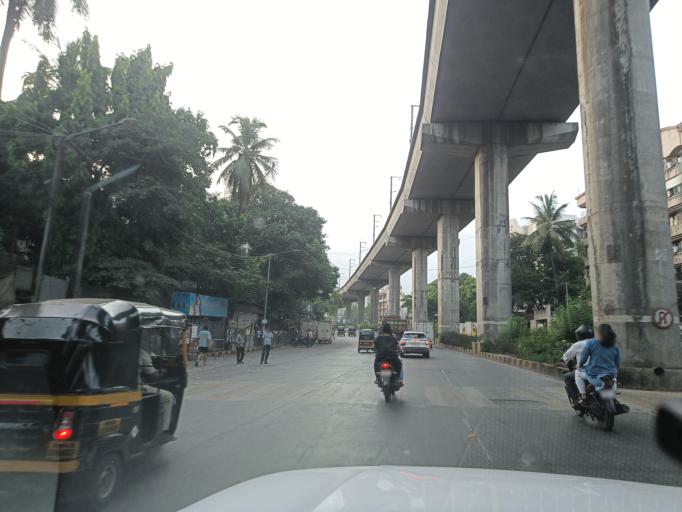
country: IN
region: Maharashtra
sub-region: Mumbai Suburban
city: Powai
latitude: 19.1155
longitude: 72.8569
